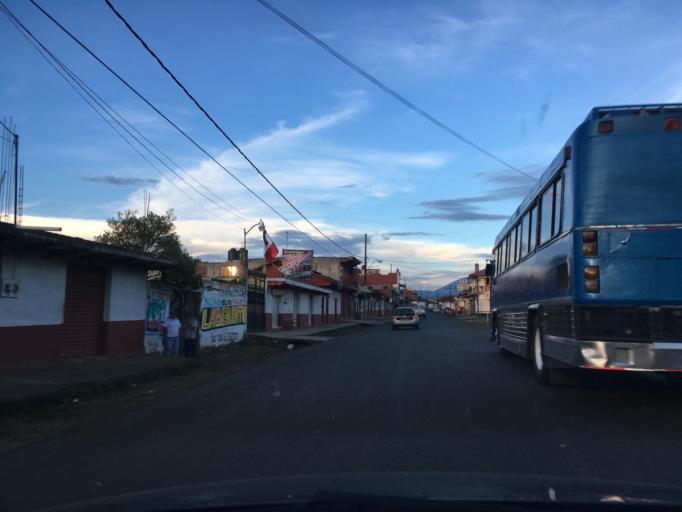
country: MX
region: Michoacan
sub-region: Salvador Escalante
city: Santa Clara del Cobre
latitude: 19.4041
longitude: -101.6445
